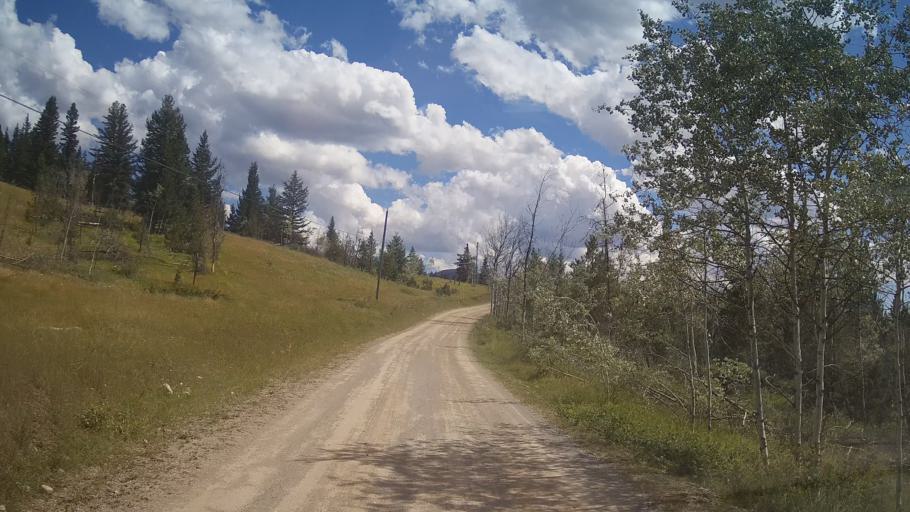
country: CA
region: British Columbia
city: Lillooet
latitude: 51.2890
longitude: -121.9745
